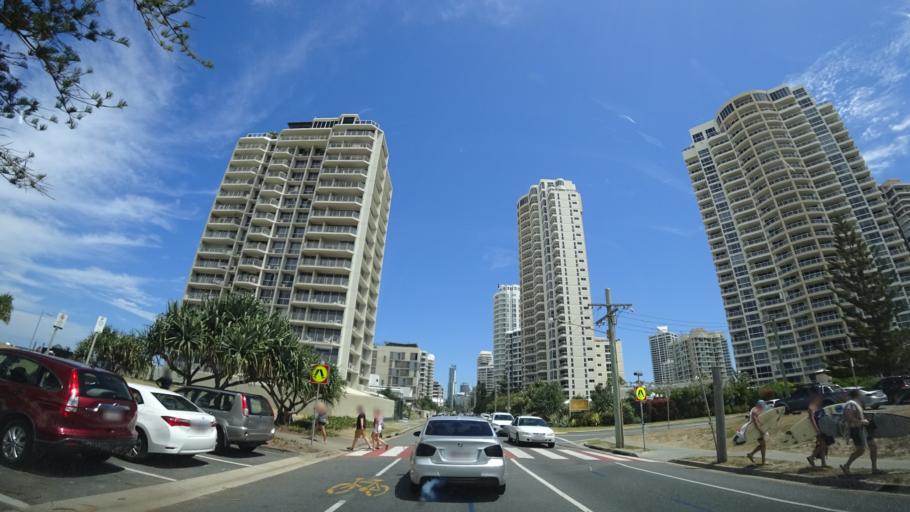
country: AU
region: Queensland
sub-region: Gold Coast
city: Main Beach
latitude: -27.9778
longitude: 153.4289
